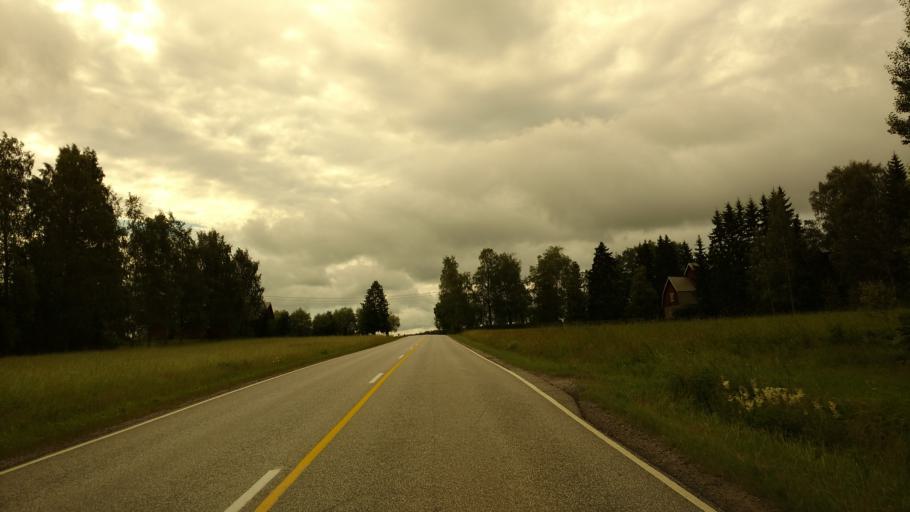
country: FI
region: Varsinais-Suomi
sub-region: Salo
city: Kuusjoki
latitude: 60.4664
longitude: 23.1612
